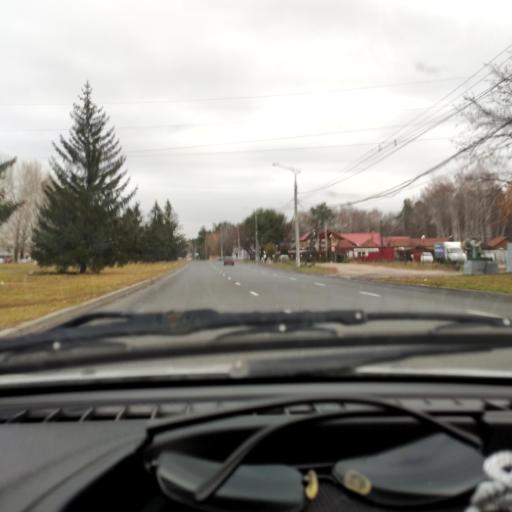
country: RU
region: Samara
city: Tol'yatti
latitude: 53.5088
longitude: 49.4548
